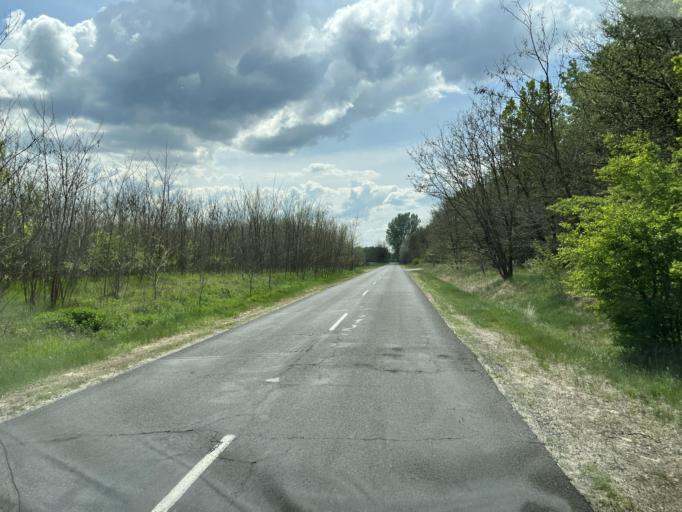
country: HU
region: Pest
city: Csemo
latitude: 47.1100
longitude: 19.6440
